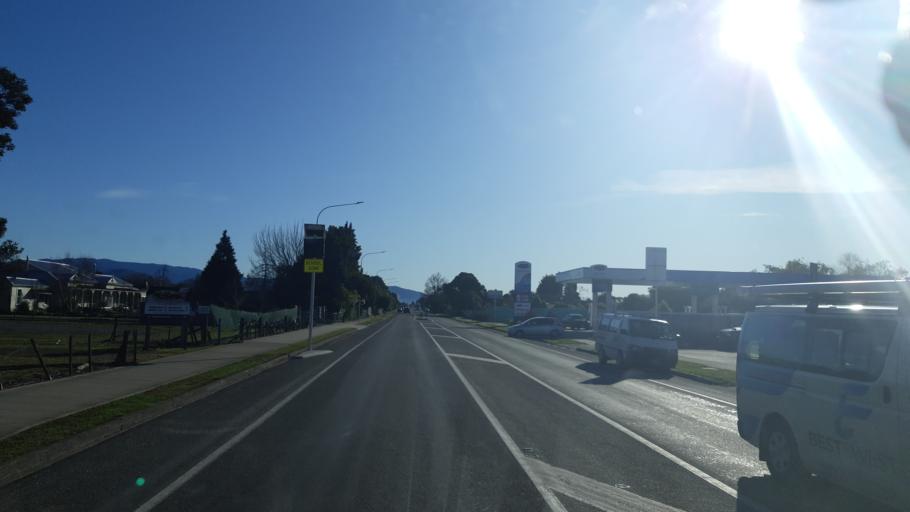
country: NZ
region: Tasman
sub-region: Tasman District
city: Motueka
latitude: -41.1312
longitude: 173.0100
